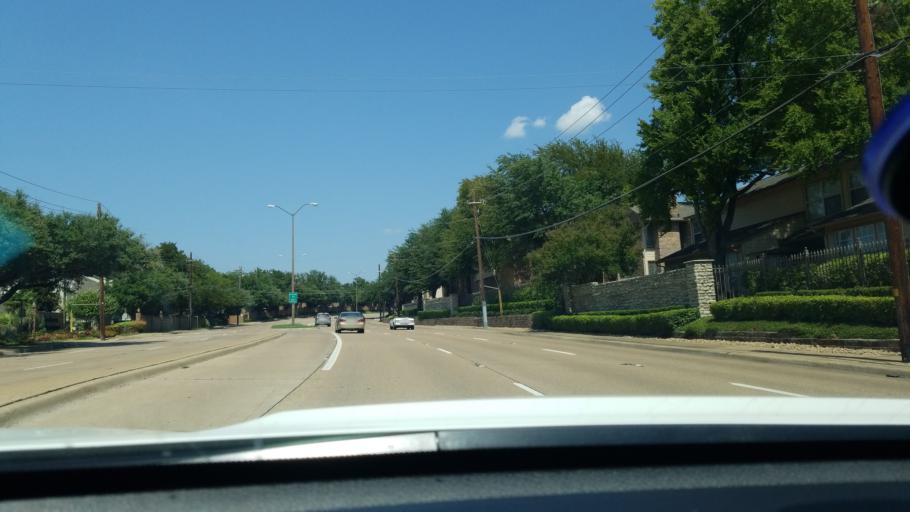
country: US
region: Texas
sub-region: Dallas County
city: Addison
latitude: 32.9609
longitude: -96.8077
